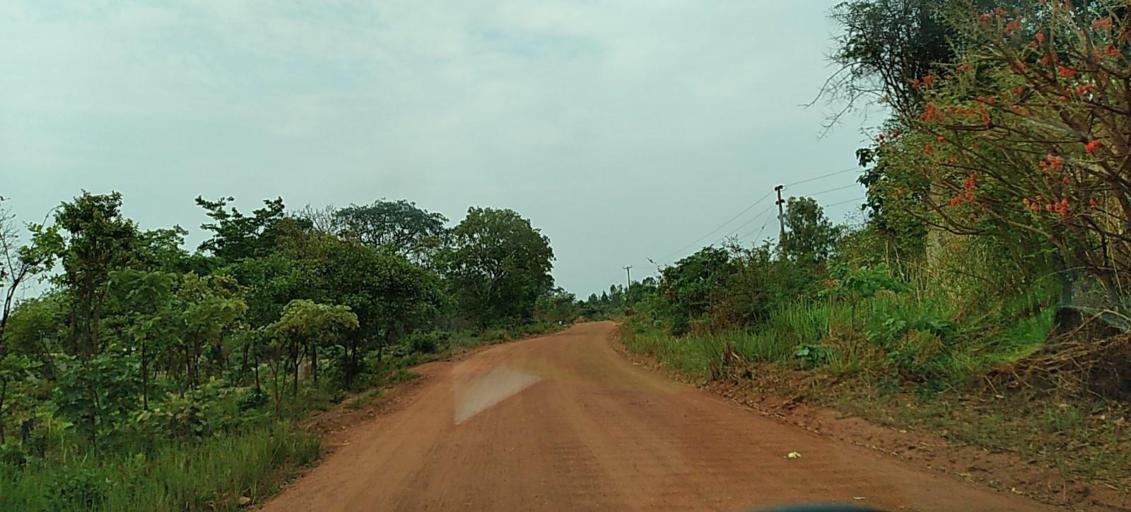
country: ZM
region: North-Western
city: Solwezi
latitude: -12.2417
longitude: 26.5120
